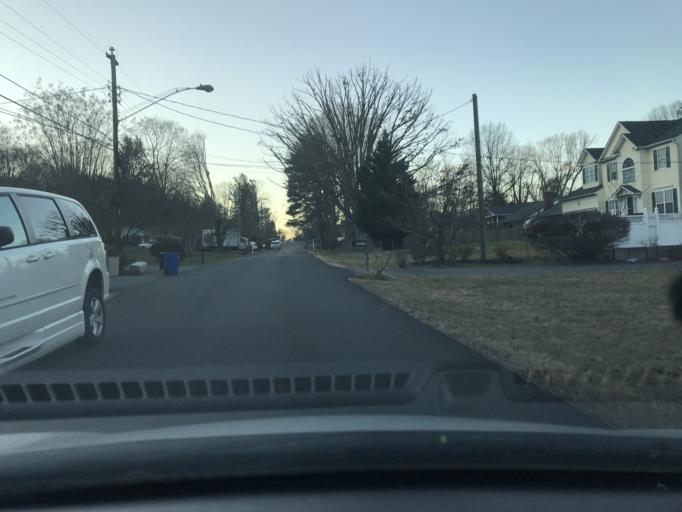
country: US
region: Virginia
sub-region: Fairfax County
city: Oakton
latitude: 38.8653
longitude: -77.3137
